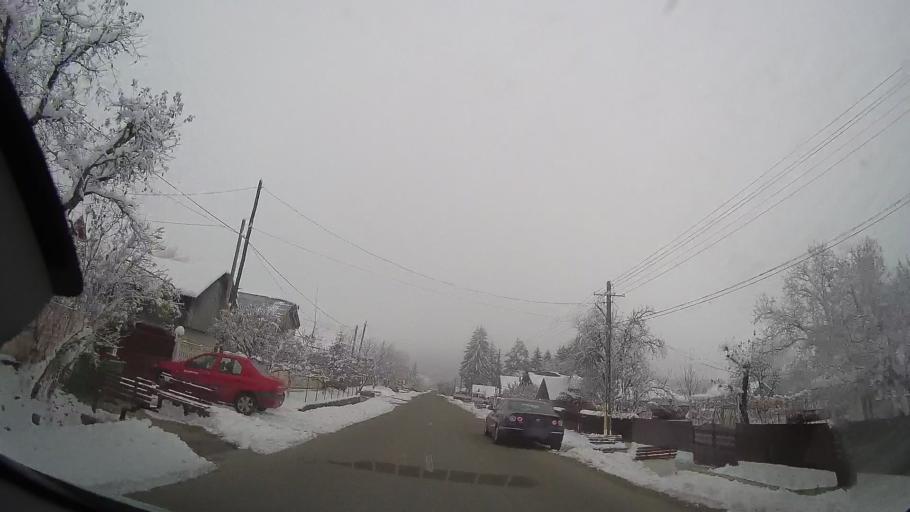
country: RO
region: Neamt
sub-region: Comuna Valea Ursului
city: Valea Ursului
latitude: 46.8526
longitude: 27.0523
